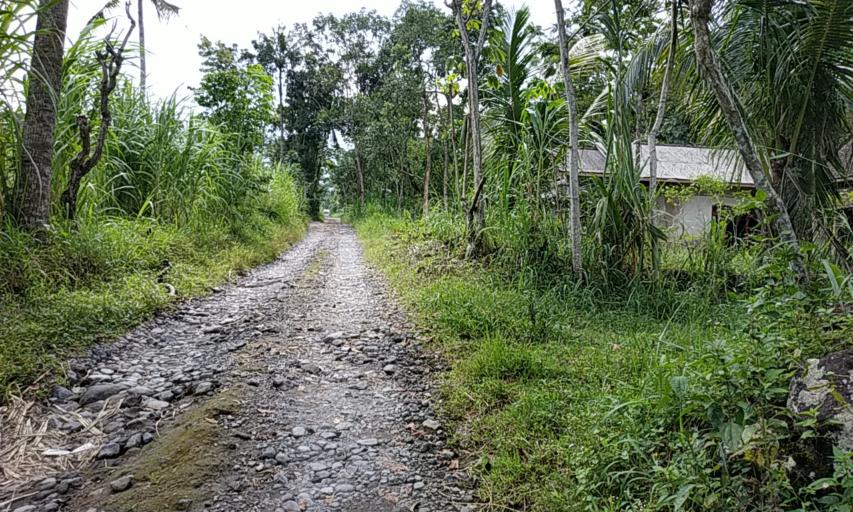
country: ID
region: Central Java
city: Jogonalan
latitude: -7.6330
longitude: 110.4868
